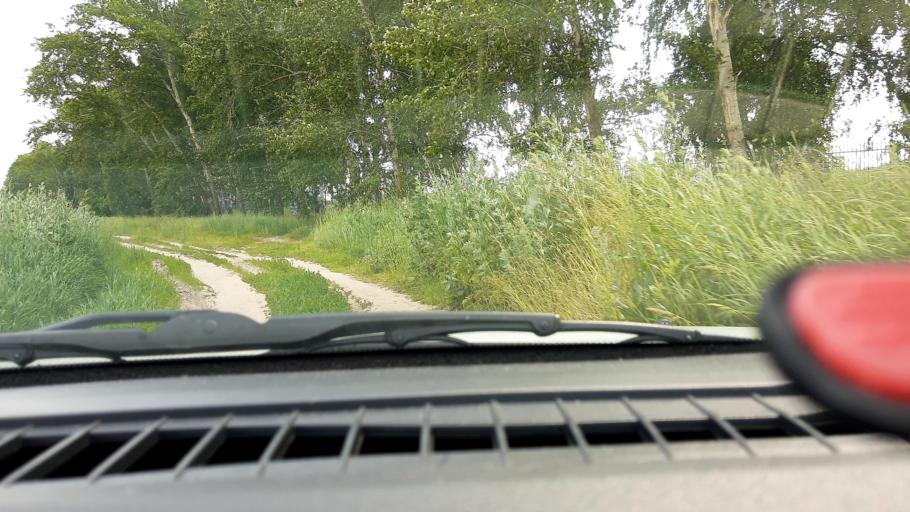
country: RU
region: Nizjnij Novgorod
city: Afonino
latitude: 56.1201
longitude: 44.0287
